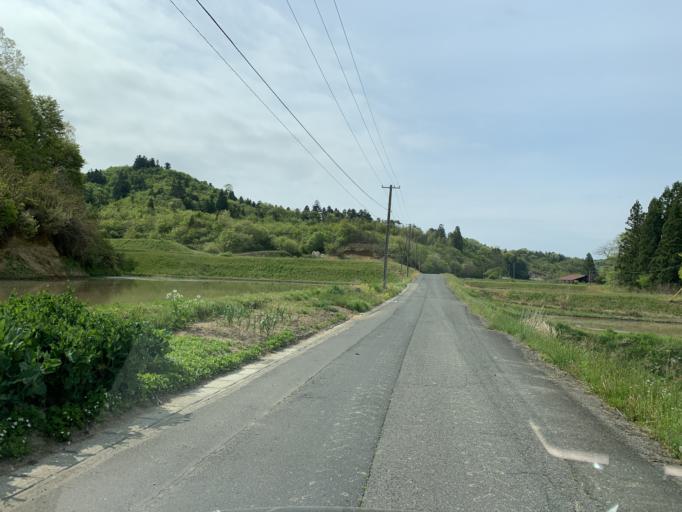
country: JP
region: Iwate
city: Ichinoseki
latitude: 38.8971
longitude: 141.0615
